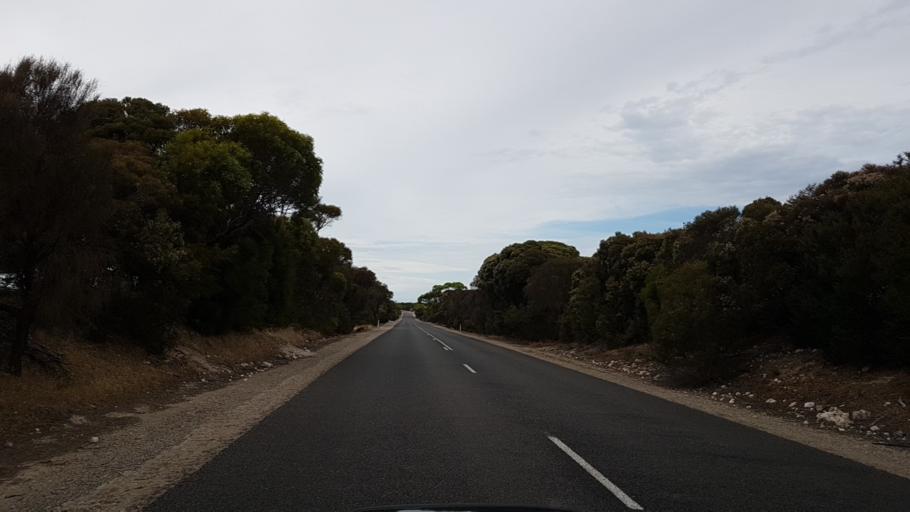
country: AU
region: South Australia
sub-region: Yorke Peninsula
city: Honiton
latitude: -34.9649
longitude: 137.1078
